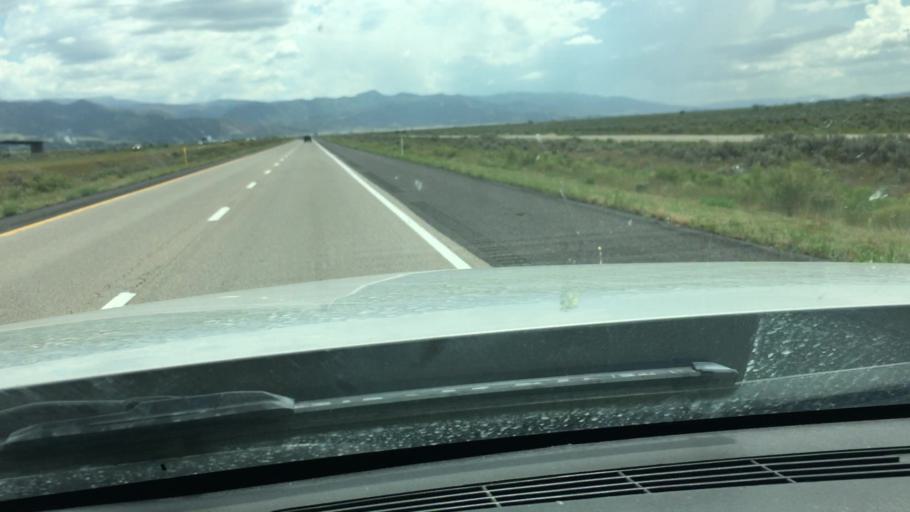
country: US
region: Utah
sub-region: Iron County
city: Parowan
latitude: 37.9381
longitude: -112.7612
